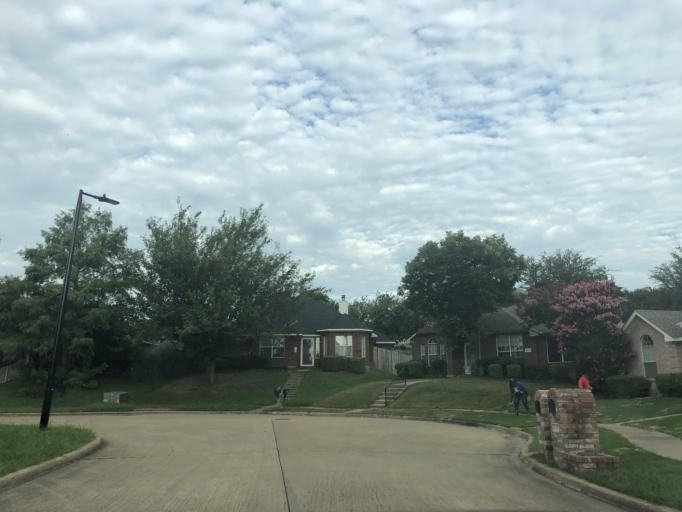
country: US
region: Texas
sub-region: Dallas County
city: Sunnyvale
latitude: 32.8437
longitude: -96.5652
